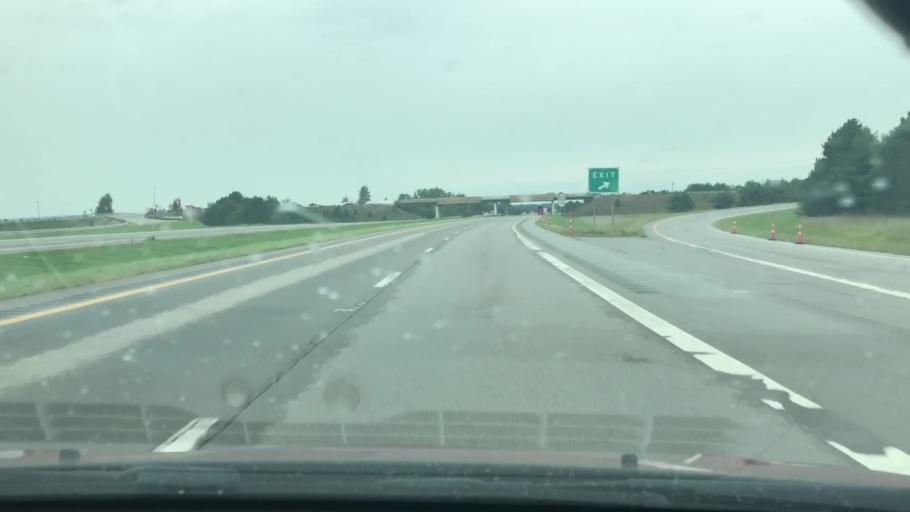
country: US
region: Ohio
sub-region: Wyandot County
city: Carey
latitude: 40.9680
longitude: -83.4821
